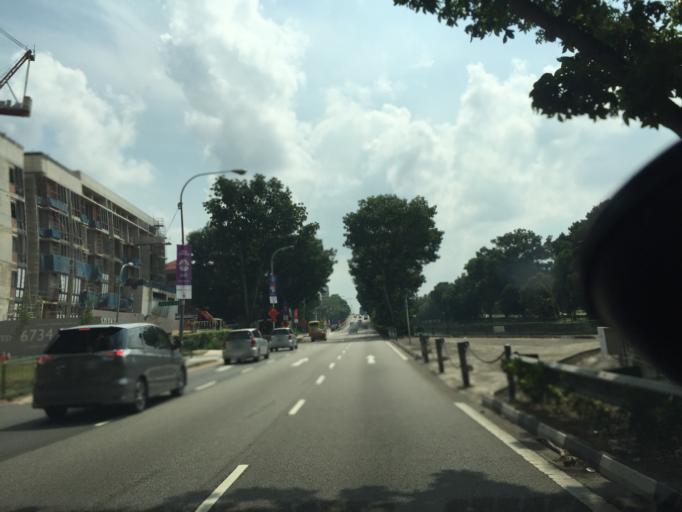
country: SG
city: Singapore
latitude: 1.3194
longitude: 103.8290
